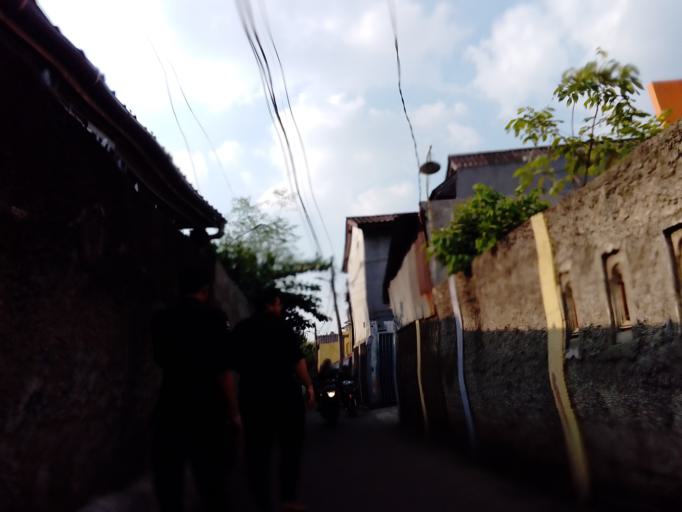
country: ID
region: Jakarta Raya
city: Jakarta
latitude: -6.2591
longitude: 106.7900
